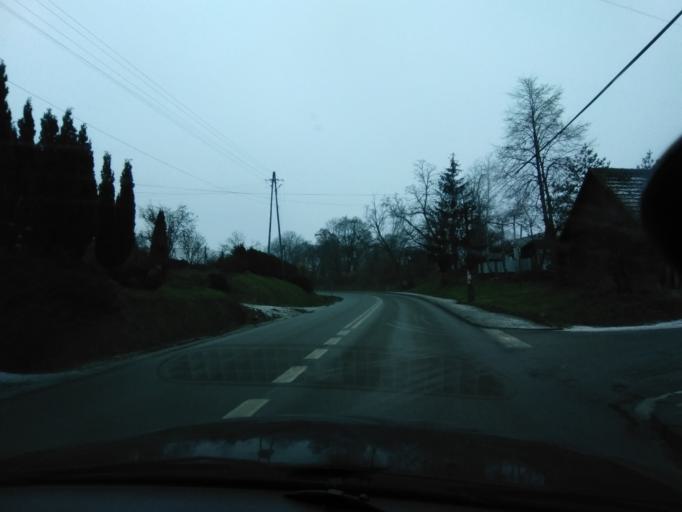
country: PL
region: Subcarpathian Voivodeship
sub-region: Powiat przeworski
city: Urzejowice
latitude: 50.0068
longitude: 22.4402
